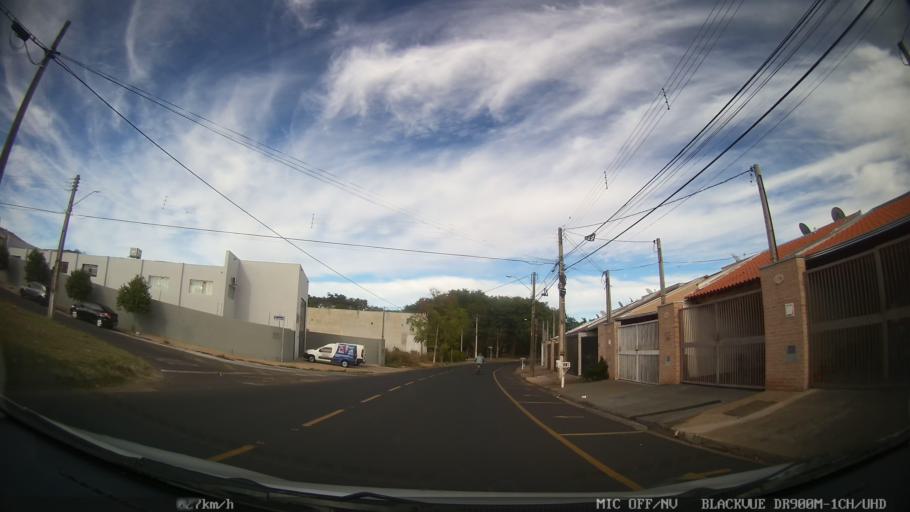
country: BR
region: Sao Paulo
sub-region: Catanduva
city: Catanduva
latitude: -21.1393
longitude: -48.9996
